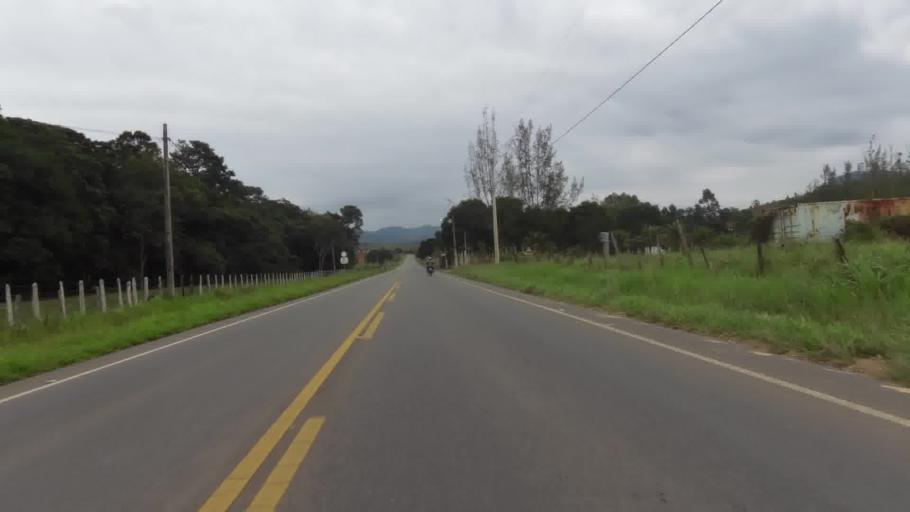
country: BR
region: Espirito Santo
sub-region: Piuma
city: Piuma
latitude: -20.8063
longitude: -40.7418
